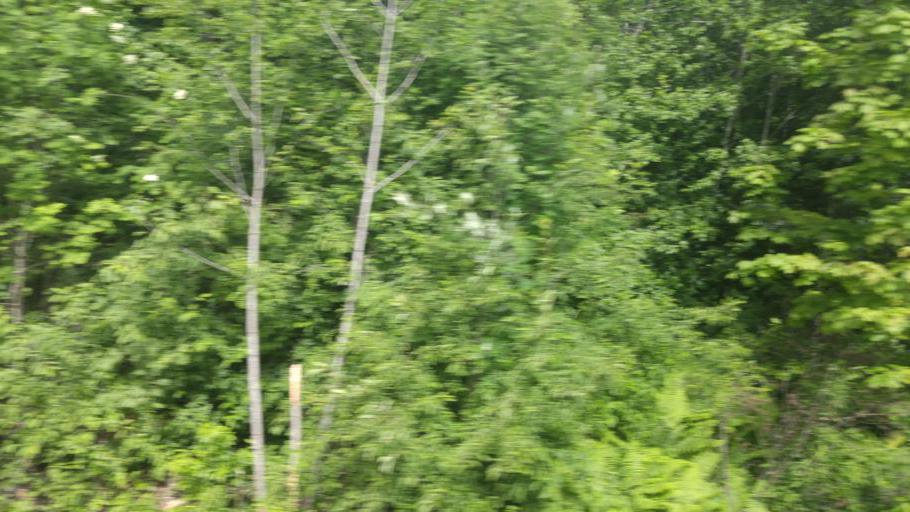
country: NO
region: Sor-Trondelag
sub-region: Trondheim
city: Trondheim
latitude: 63.3976
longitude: 10.3848
